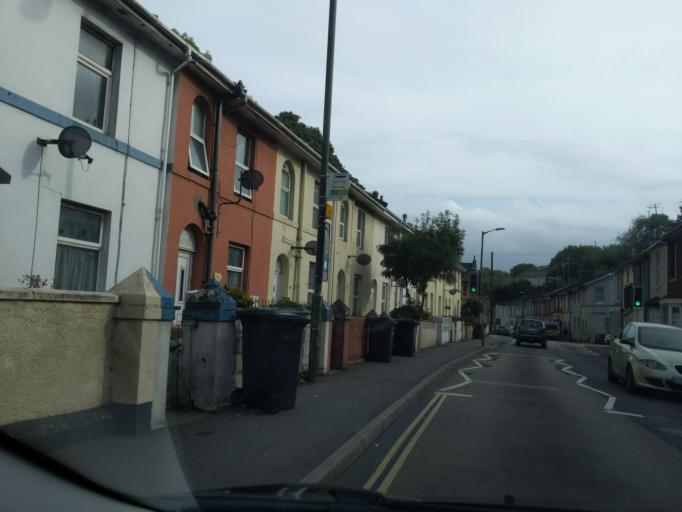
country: GB
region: England
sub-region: Borough of Torbay
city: Torquay
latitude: 50.4849
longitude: -3.5391
